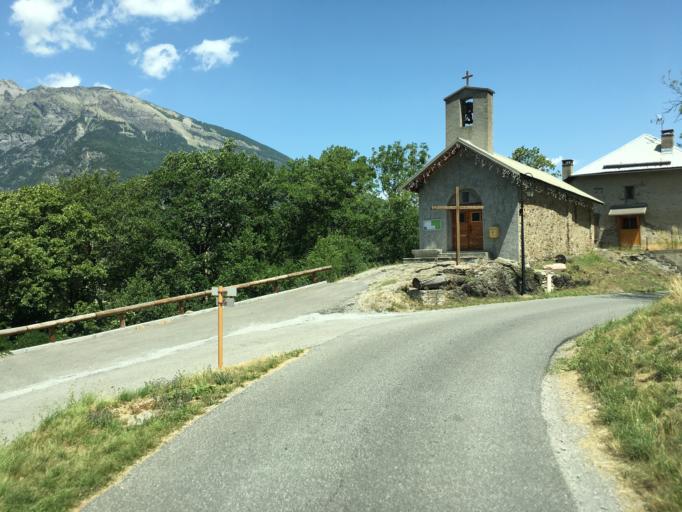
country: FR
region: Provence-Alpes-Cote d'Azur
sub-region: Departement des Hautes-Alpes
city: Guillestre
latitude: 44.6299
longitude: 6.5742
